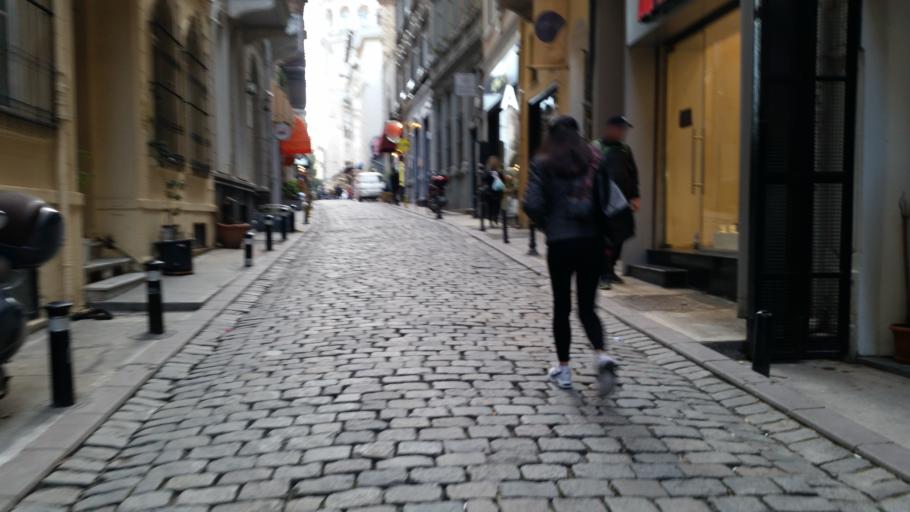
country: TR
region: Istanbul
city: Eminoenue
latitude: 41.0268
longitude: 28.9753
